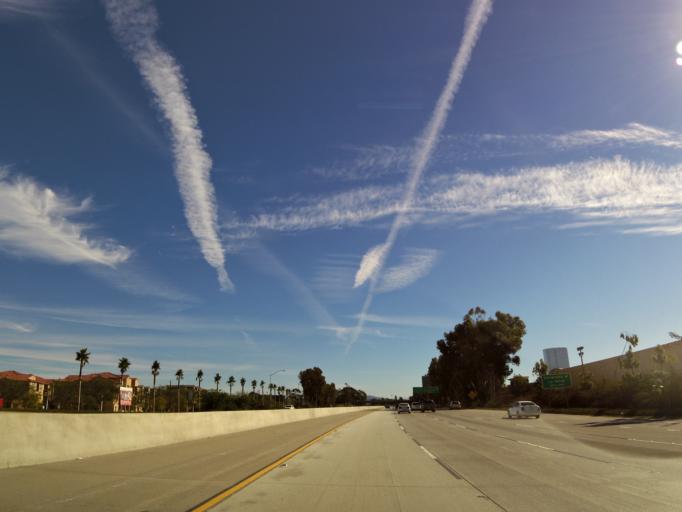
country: US
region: California
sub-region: Ventura County
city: El Rio
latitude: 34.2367
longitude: -119.1772
